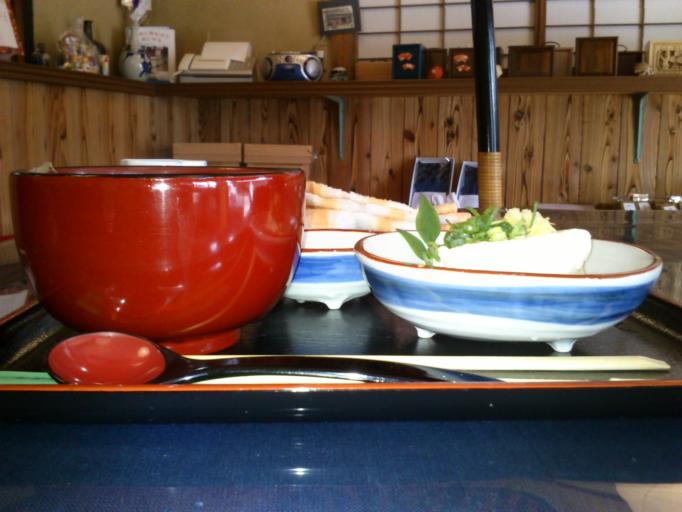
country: JP
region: Tokushima
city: Wakimachi
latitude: 34.0680
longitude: 134.1467
